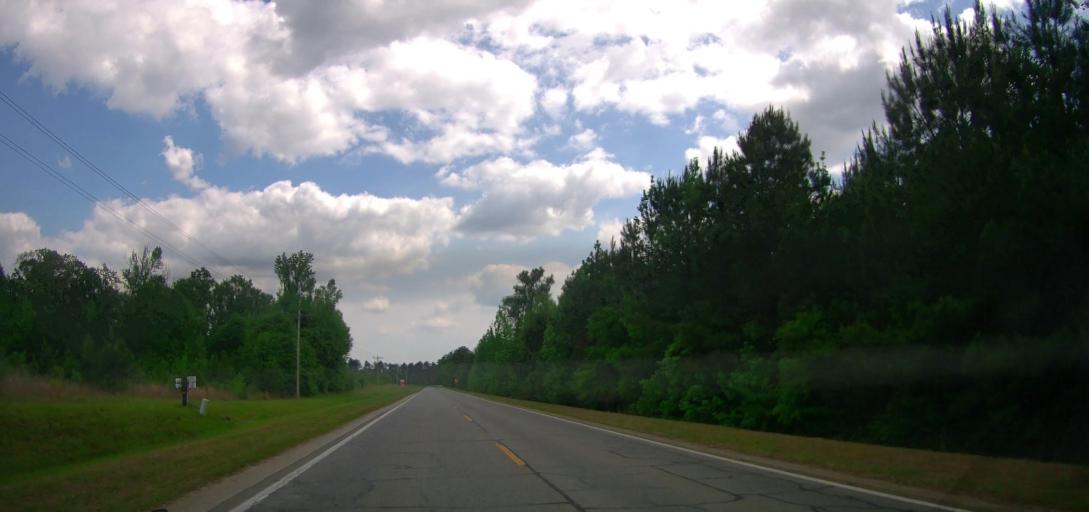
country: US
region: Georgia
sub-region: Laurens County
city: East Dublin
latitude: 32.4843
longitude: -82.8205
